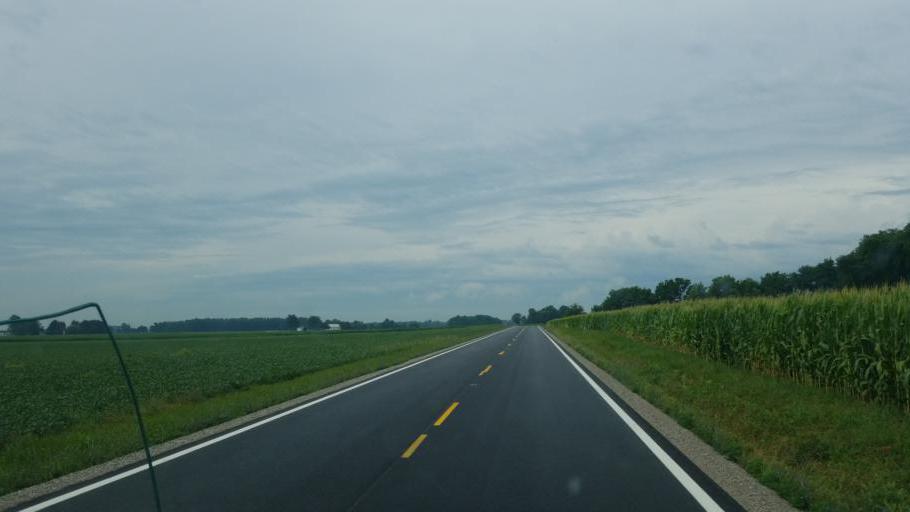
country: US
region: Ohio
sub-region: Defiance County
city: Hicksville
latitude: 41.3471
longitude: -84.6758
